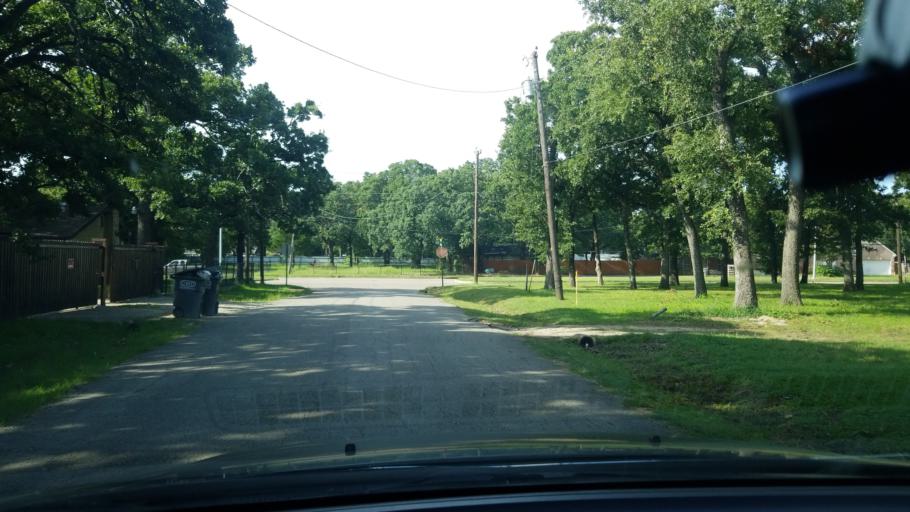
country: US
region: Texas
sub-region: Dallas County
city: Balch Springs
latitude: 32.7200
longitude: -96.6337
